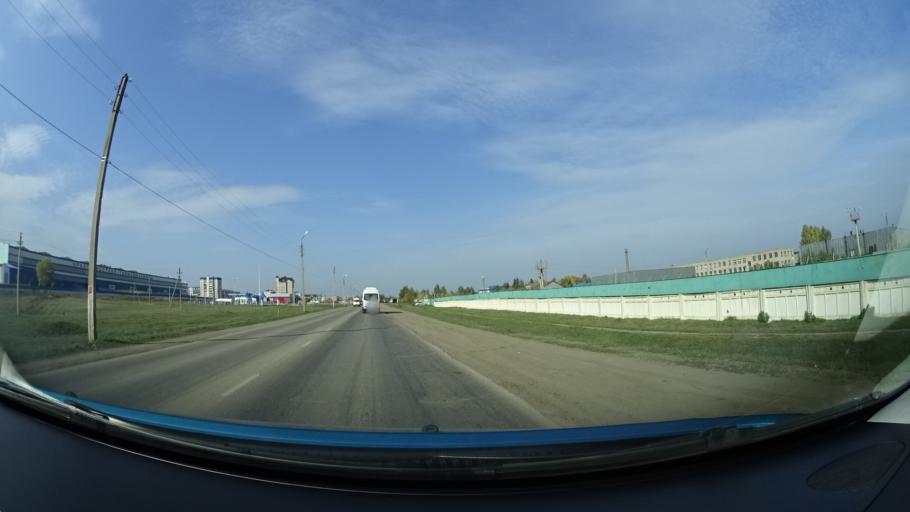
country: RU
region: Bashkortostan
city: Tuymazy
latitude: 54.5936
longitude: 53.7228
